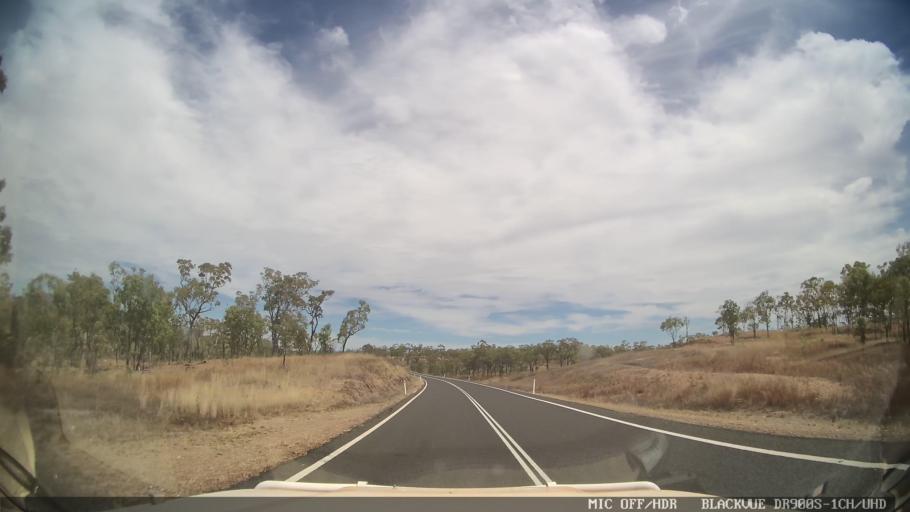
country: AU
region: Queensland
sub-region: Cairns
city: Port Douglas
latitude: -16.1417
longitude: 144.7701
